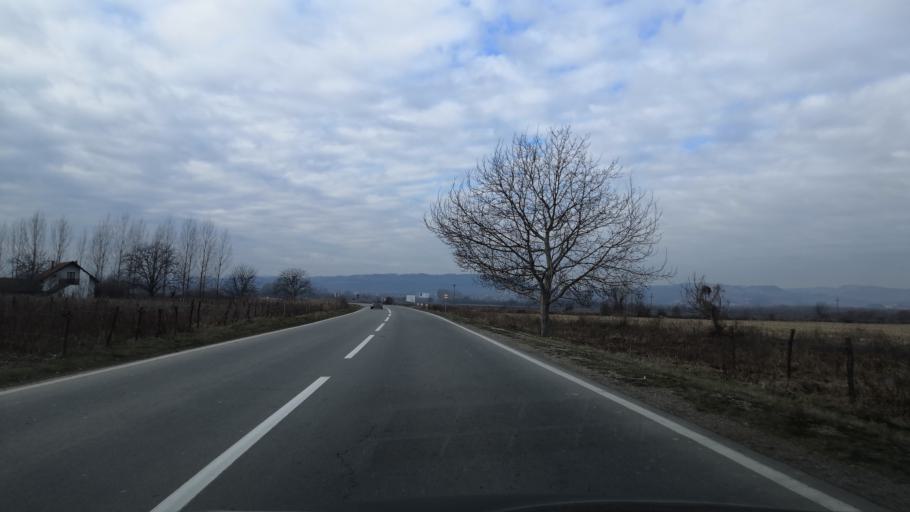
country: RS
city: Lipnicki Sor
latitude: 44.5722
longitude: 19.2182
